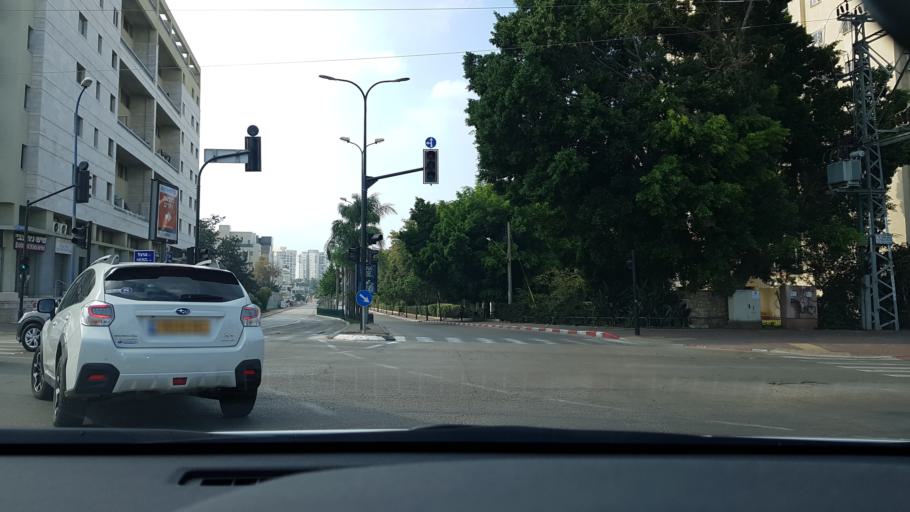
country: IL
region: Central District
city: Mazkeret Batya
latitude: 31.8834
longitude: 34.8168
